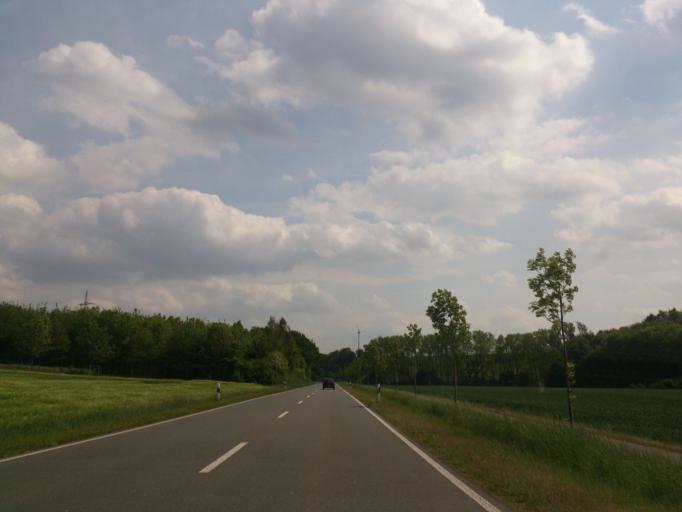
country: DE
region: North Rhine-Westphalia
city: Bad Lippspringe
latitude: 51.7522
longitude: 8.8345
